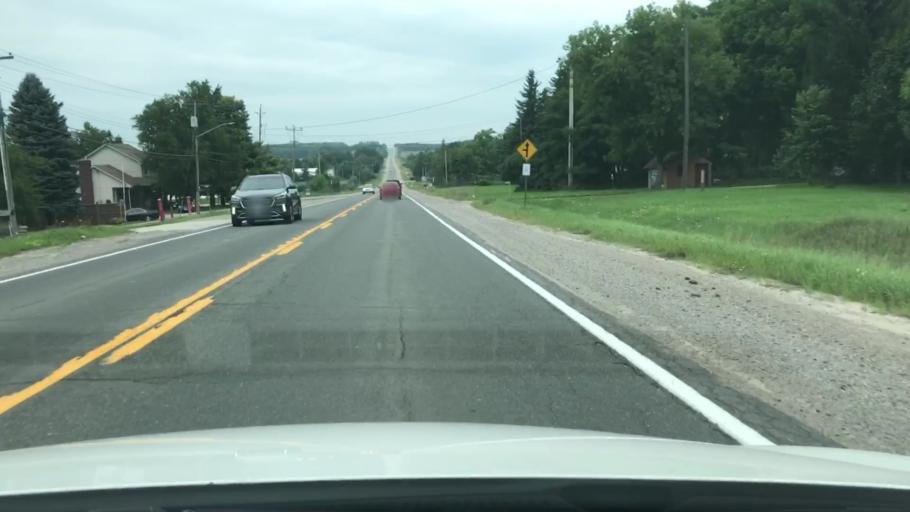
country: CA
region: Ontario
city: Innisfil
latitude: 44.2565
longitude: -79.6022
